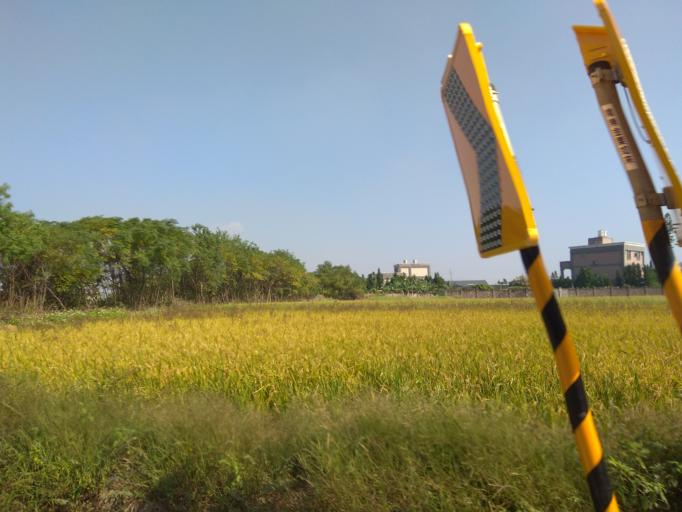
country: TW
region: Taiwan
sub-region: Hsinchu
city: Zhubei
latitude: 24.9897
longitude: 121.0740
